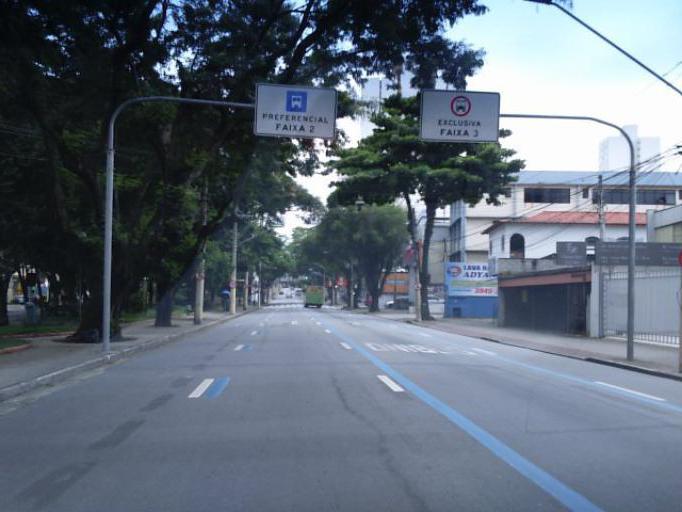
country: BR
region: Sao Paulo
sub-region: Sao Jose Dos Campos
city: Sao Jose dos Campos
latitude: -23.1951
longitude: -45.8909
